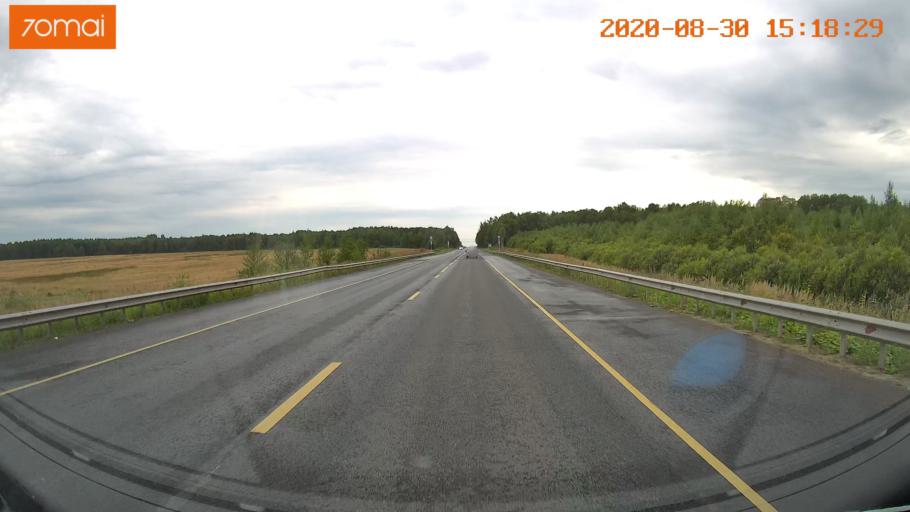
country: RU
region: Ivanovo
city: Rodniki
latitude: 57.1227
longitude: 41.7932
